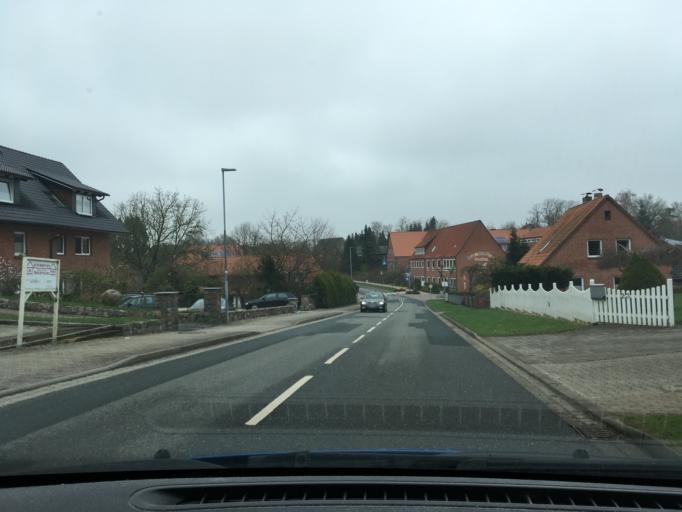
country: DE
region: Lower Saxony
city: Neetze
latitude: 53.2611
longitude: 10.6270
